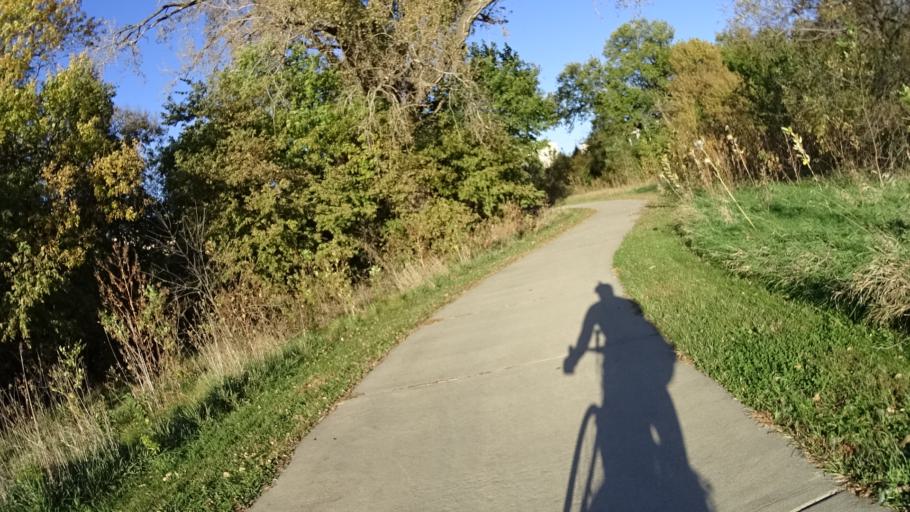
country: US
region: Nebraska
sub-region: Sarpy County
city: Papillion
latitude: 41.1442
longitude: -96.0663
